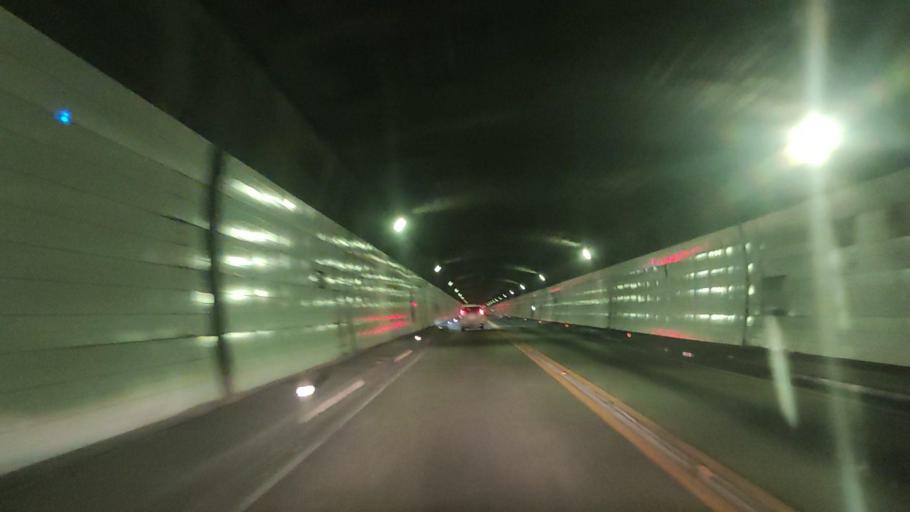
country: JP
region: Kumamoto
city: Hitoyoshi
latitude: 32.1030
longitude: 130.8048
